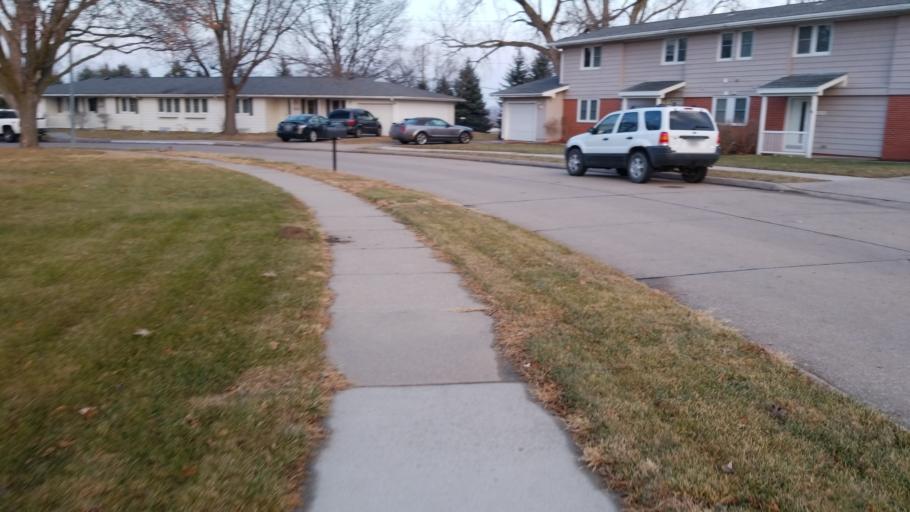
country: US
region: Nebraska
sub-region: Sarpy County
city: Offutt Air Force Base
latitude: 41.1205
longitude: -95.9484
